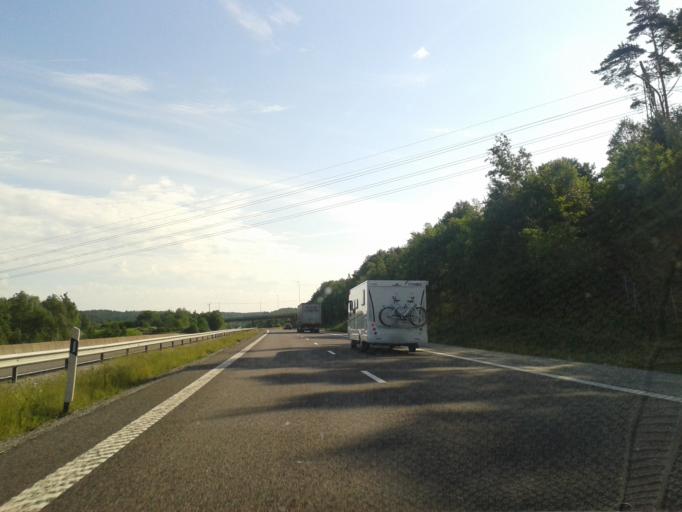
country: SE
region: Vaestra Goetaland
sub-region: Stenungsunds Kommun
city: Stora Hoga
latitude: 58.0542
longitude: 11.8735
